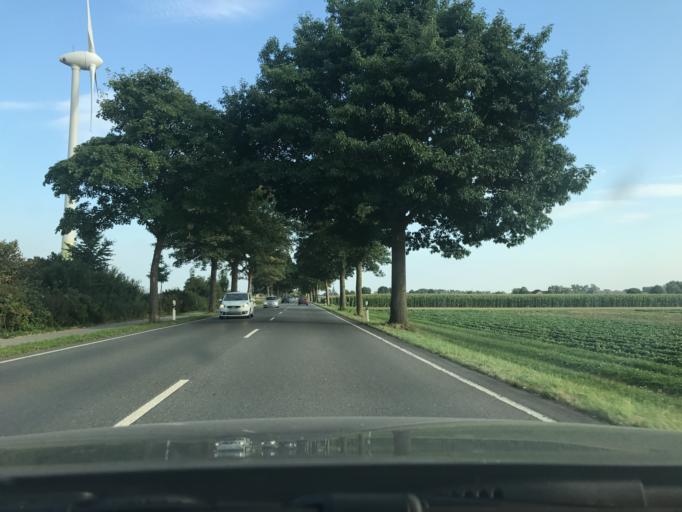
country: DE
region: North Rhine-Westphalia
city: Geldern
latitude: 51.4720
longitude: 6.3529
